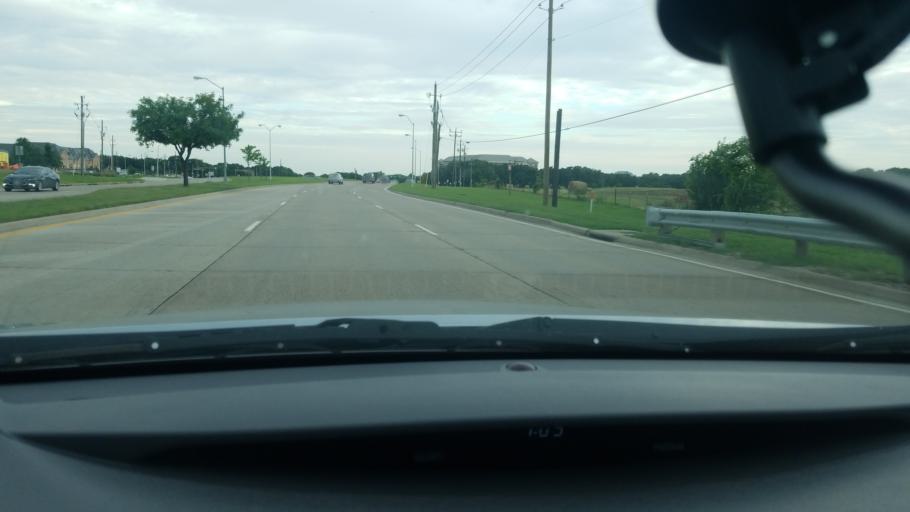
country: US
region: Texas
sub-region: Collin County
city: Frisco
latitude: 33.0747
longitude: -96.7961
